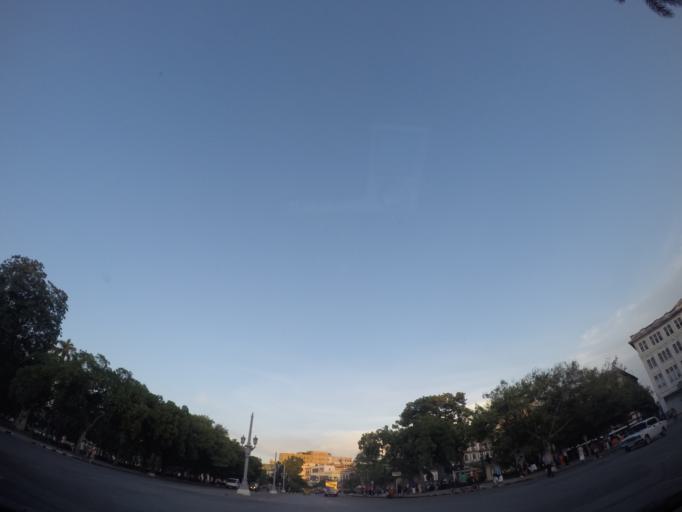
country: CU
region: La Habana
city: Centro Habana
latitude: 23.1325
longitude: -82.3602
